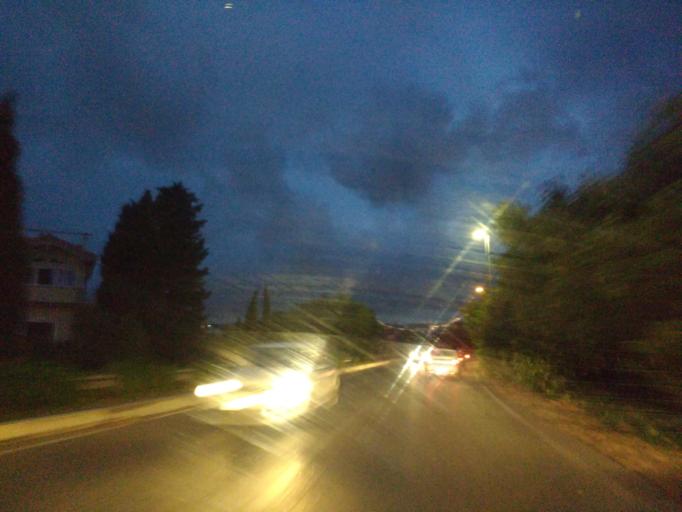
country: IT
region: Latium
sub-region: Citta metropolitana di Roma Capitale
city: Anzio
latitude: 41.4563
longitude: 12.6210
